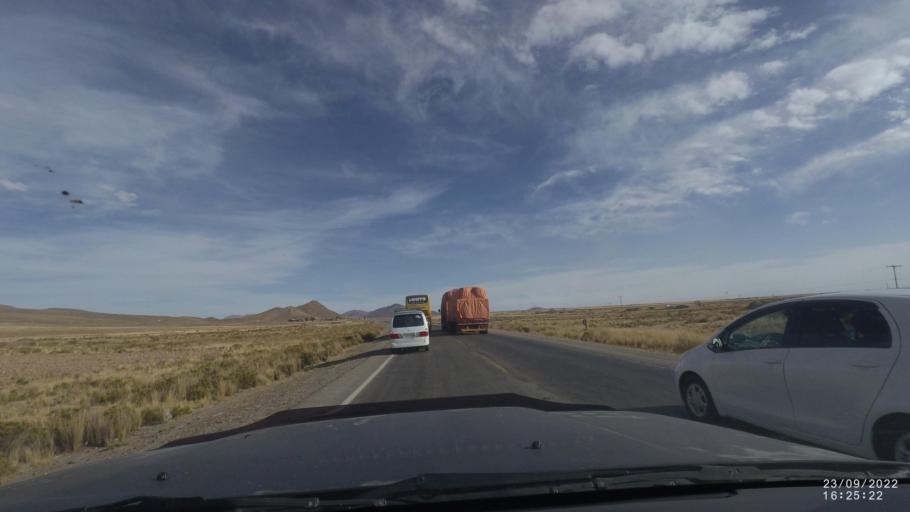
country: BO
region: Oruro
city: Machacamarca
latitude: -18.0914
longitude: -67.0105
